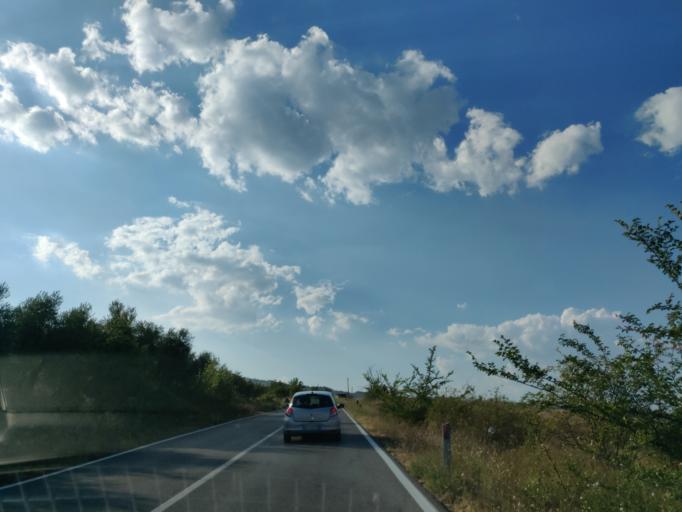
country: IT
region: Tuscany
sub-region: Provincia di Siena
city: Piancastagnaio
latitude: 42.8316
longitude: 11.7195
